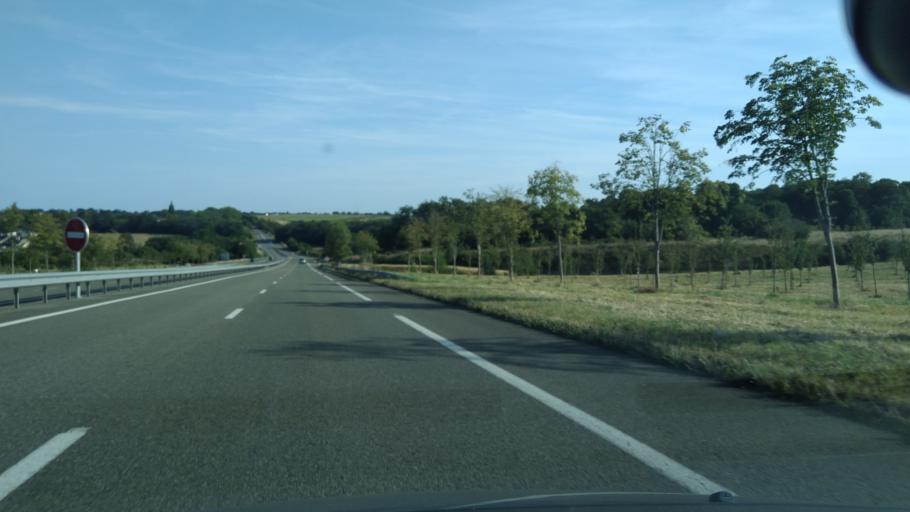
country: FR
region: Pays de la Loire
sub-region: Departement de la Mayenne
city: Entrammes
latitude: 48.0034
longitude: -0.7250
